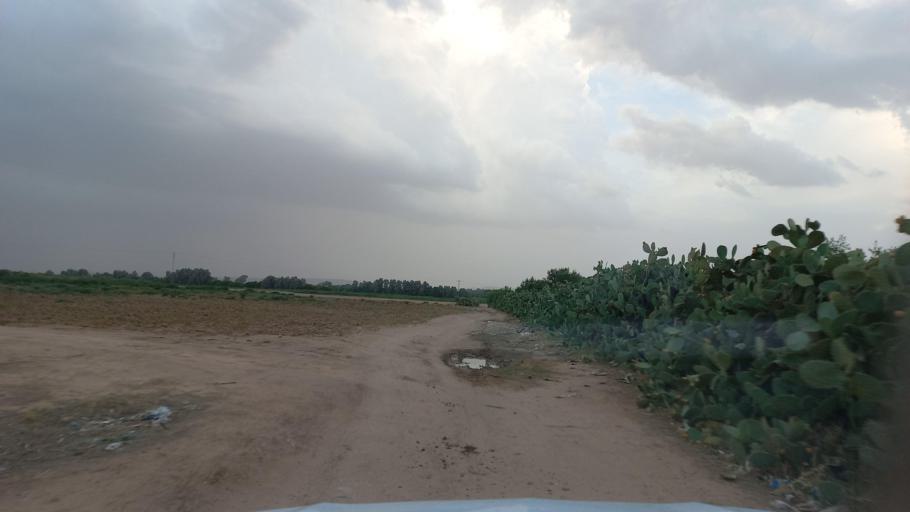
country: TN
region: Al Qasrayn
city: Kasserine
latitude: 35.2764
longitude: 9.0588
